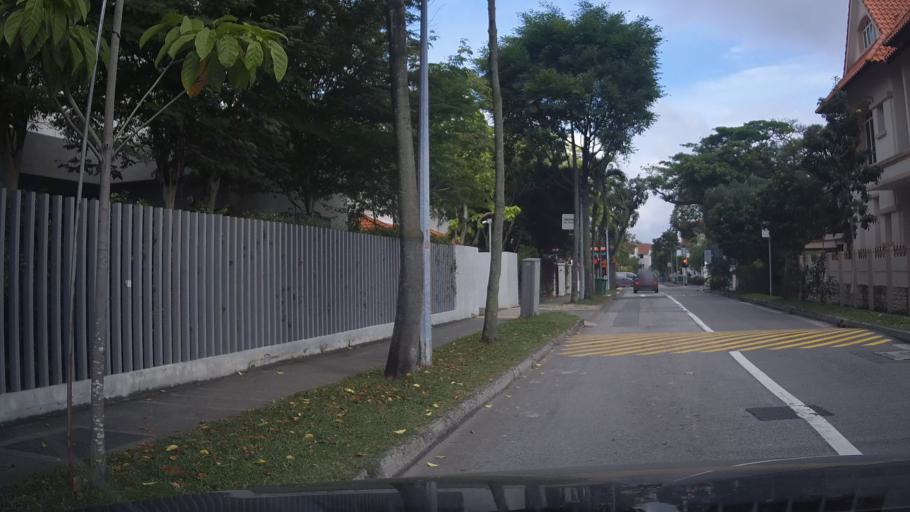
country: SG
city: Singapore
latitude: 1.3002
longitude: 103.8941
